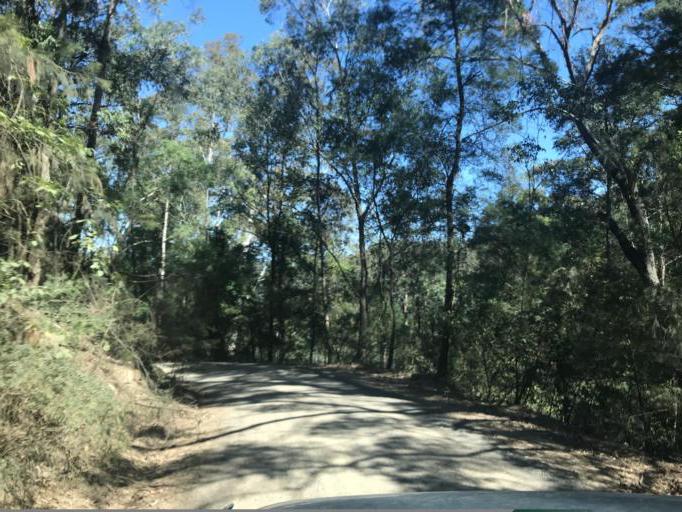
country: AU
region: New South Wales
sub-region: Wyong Shire
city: Little Jilliby
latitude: -33.1528
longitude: 151.0809
